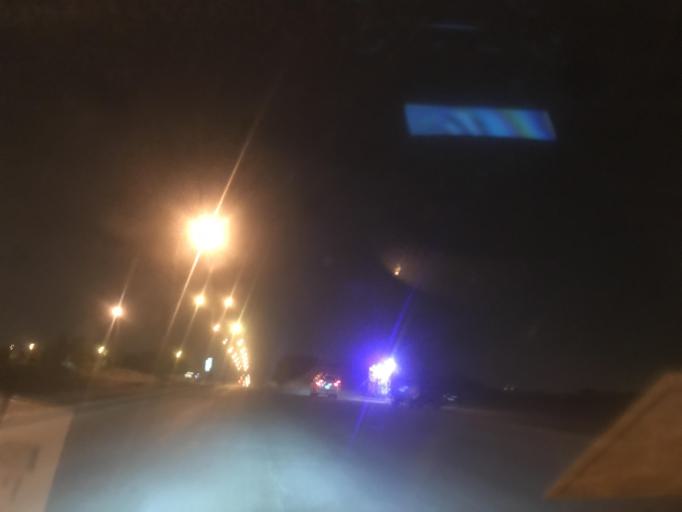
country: SA
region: Ar Riyad
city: Riyadh
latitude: 24.8117
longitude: 46.5878
